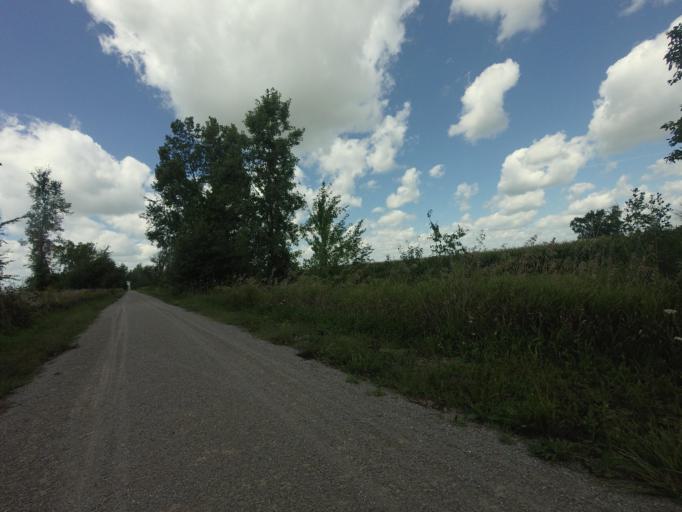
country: CA
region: Ontario
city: North Perth
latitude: 43.5786
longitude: -81.0537
